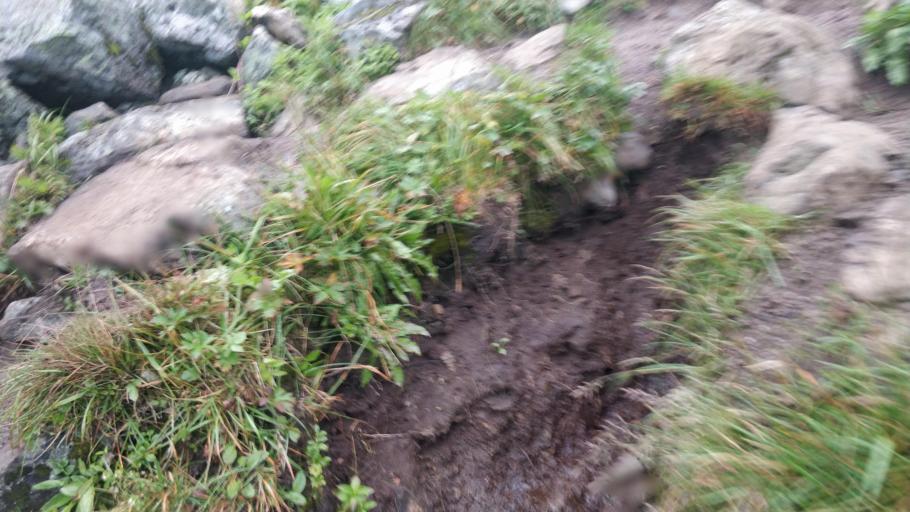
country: NO
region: Nordland
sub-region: Vagan
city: Kabelvag
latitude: 68.1777
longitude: 14.2277
